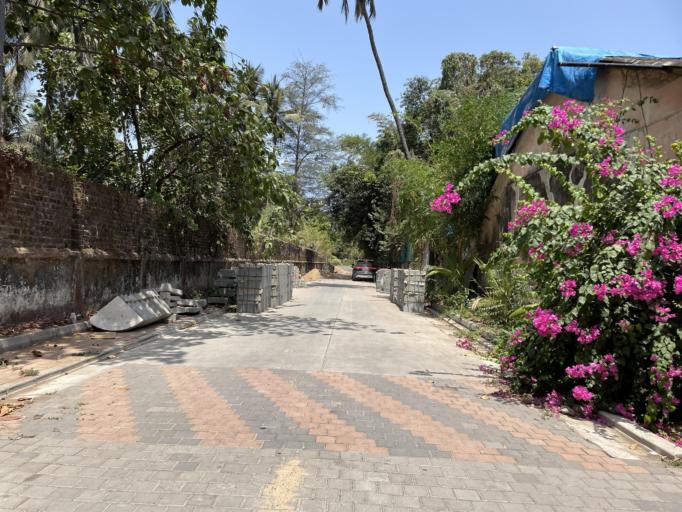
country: IN
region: Daman and Diu
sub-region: Daman District
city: Daman
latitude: 20.4072
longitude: 72.8321
